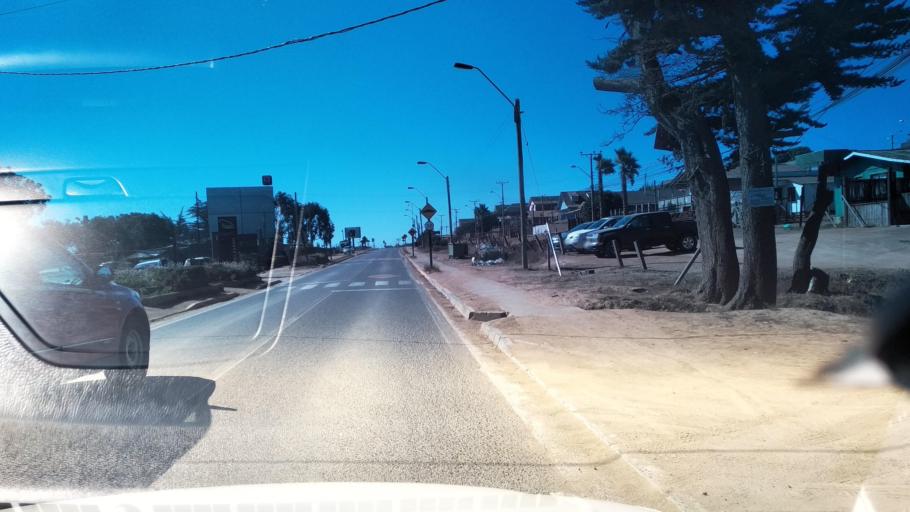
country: CL
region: O'Higgins
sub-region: Provincia de Colchagua
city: Santa Cruz
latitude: -34.4094
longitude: -72.0267
